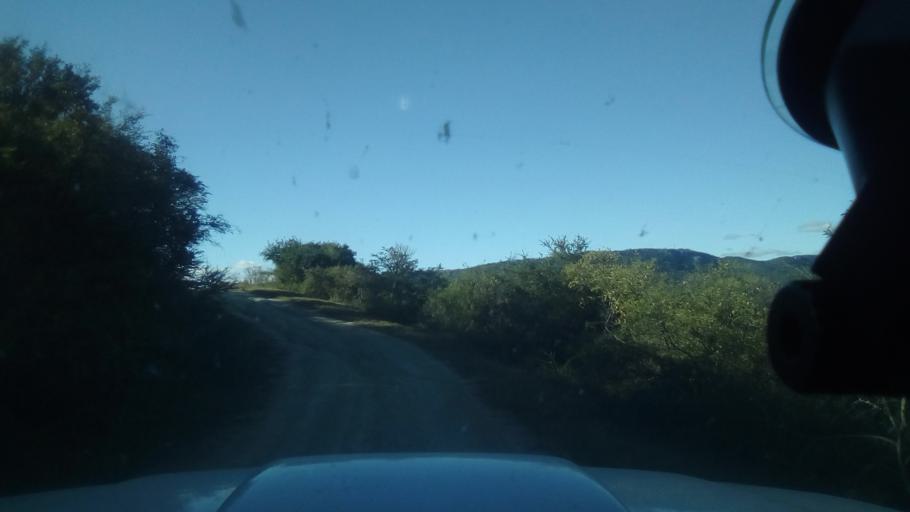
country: ZA
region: Eastern Cape
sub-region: Buffalo City Metropolitan Municipality
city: Bhisho
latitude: -32.7343
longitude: 27.3467
